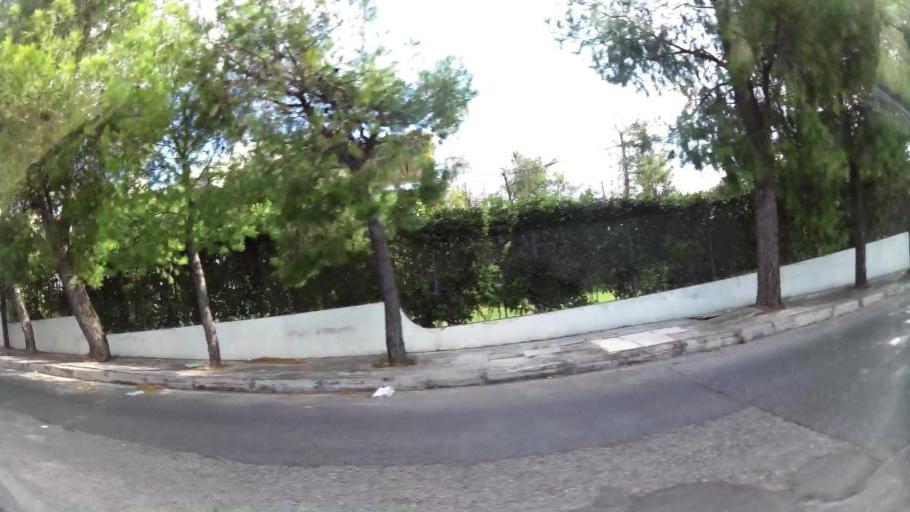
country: GR
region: Attica
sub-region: Nomarchia Anatolikis Attikis
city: Thrakomakedones
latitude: 38.1195
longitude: 23.7603
